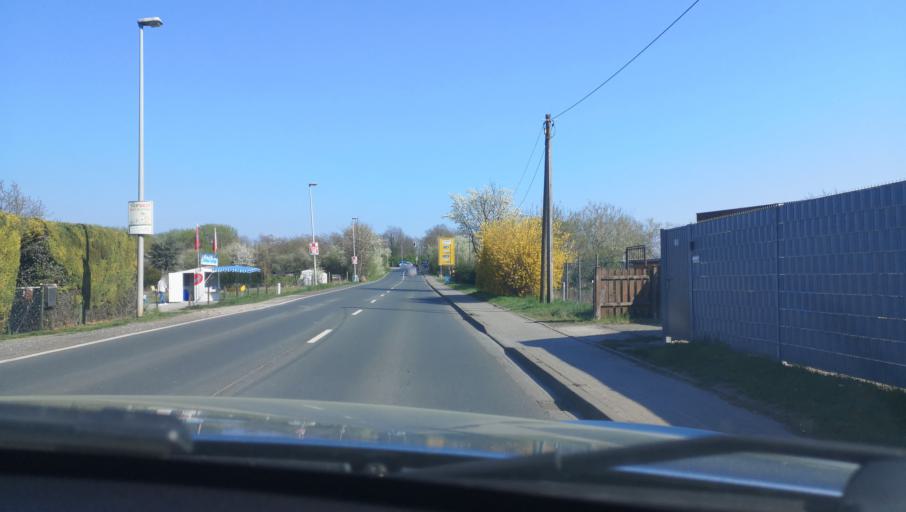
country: DE
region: Saxony-Anhalt
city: Diesdorf
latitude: 52.0832
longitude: 11.5851
